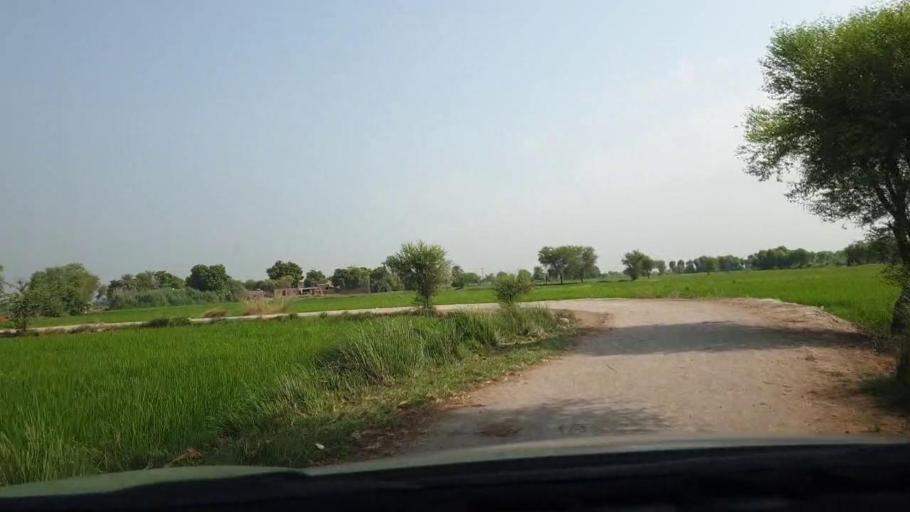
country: PK
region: Sindh
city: Goth Garelo
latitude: 27.4571
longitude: 68.1224
